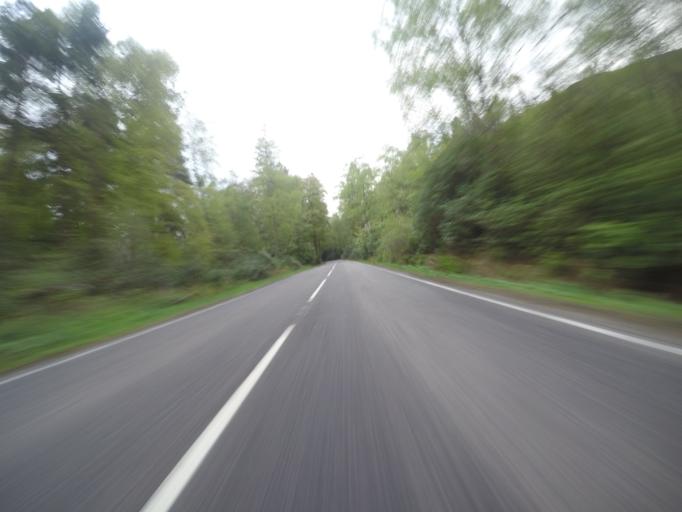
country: GB
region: Scotland
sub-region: Highland
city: Spean Bridge
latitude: 56.9503
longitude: -4.9180
